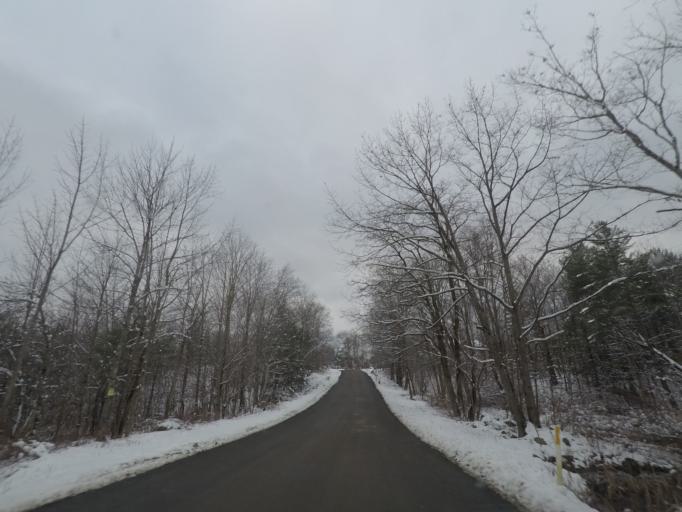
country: US
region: New York
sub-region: Rensselaer County
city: Averill Park
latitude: 42.6635
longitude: -73.5355
